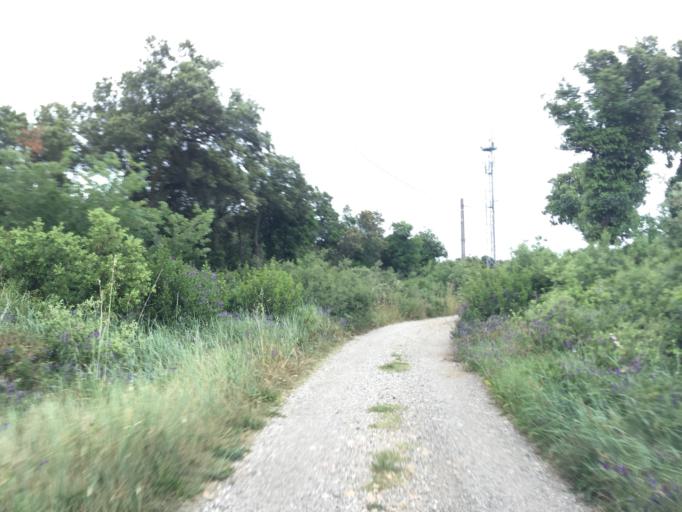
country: FR
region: Provence-Alpes-Cote d'Azur
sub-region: Departement du Vaucluse
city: Orange
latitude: 44.1188
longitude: 4.8301
